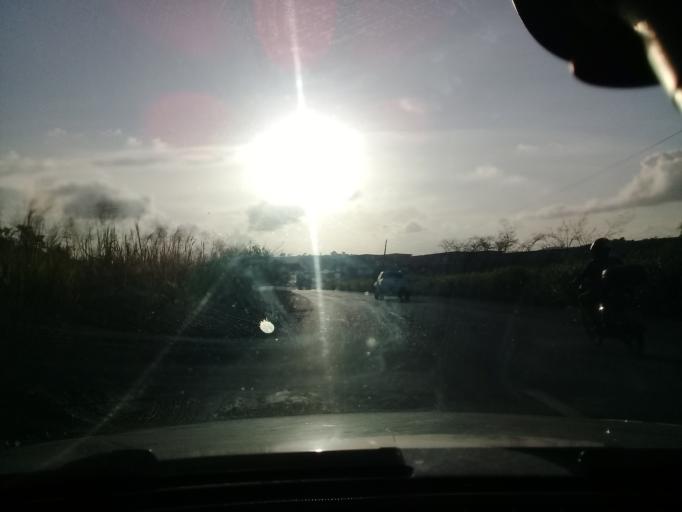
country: BR
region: Pernambuco
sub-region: Vitoria De Santo Antao
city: Vitoria de Santo Antao
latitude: -8.1142
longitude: -35.2385
